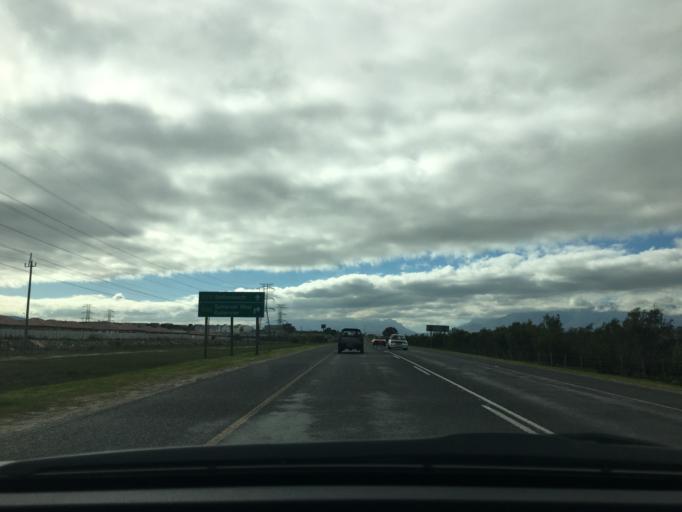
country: ZA
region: Western Cape
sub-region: Cape Winelands District Municipality
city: Stellenbosch
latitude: -34.0254
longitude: 18.7369
